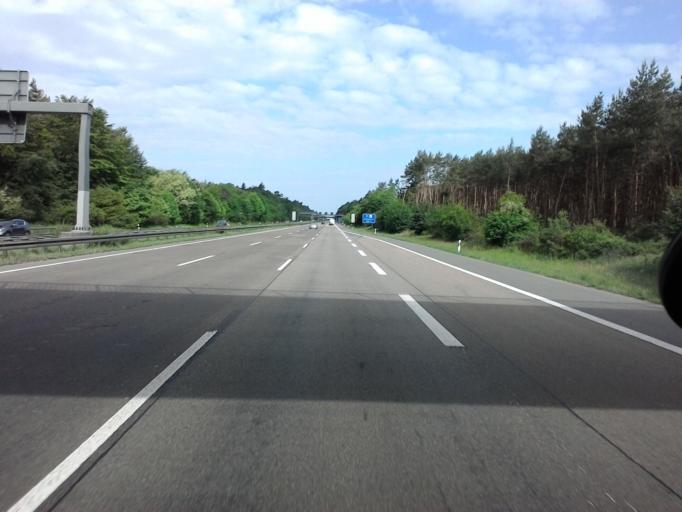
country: DE
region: Hesse
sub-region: Regierungsbezirk Darmstadt
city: Seligenstadt
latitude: 49.9968
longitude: 9.0066
